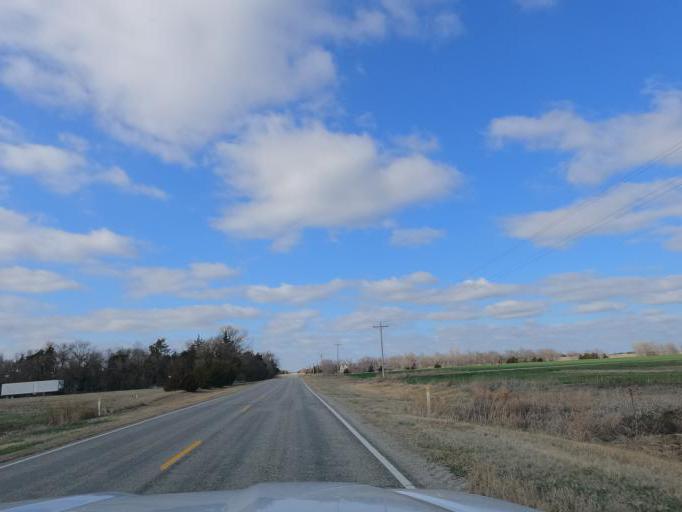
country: US
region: Kansas
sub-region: McPherson County
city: Inman
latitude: 38.2056
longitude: -97.8483
